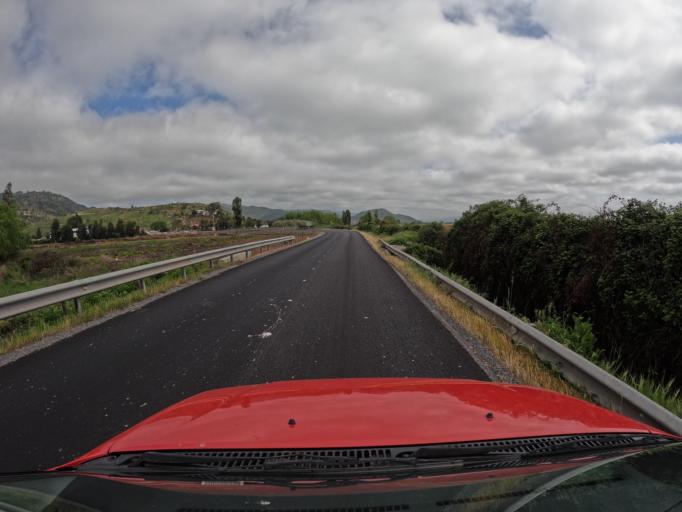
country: CL
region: O'Higgins
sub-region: Provincia de Colchagua
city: Santa Cruz
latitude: -34.6640
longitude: -71.3953
